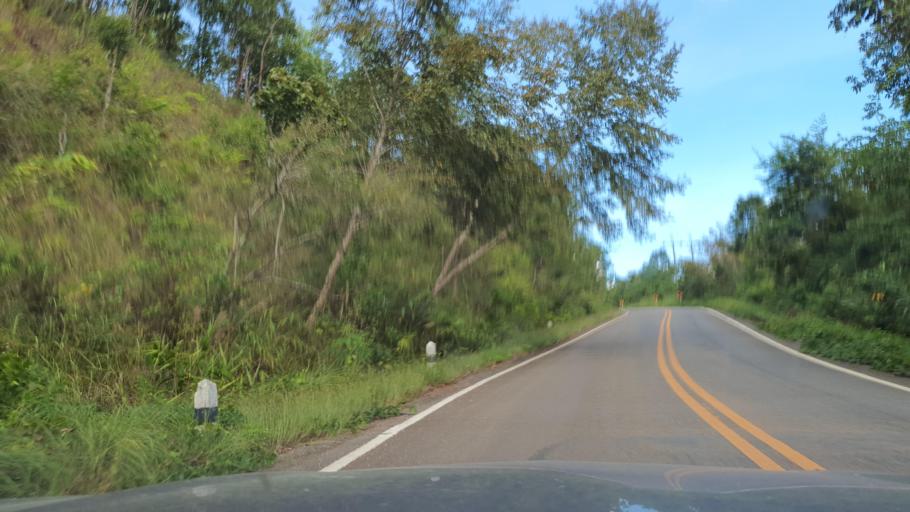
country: TH
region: Chiang Rai
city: Wiang Pa Pao
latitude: 19.3109
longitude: 99.4215
